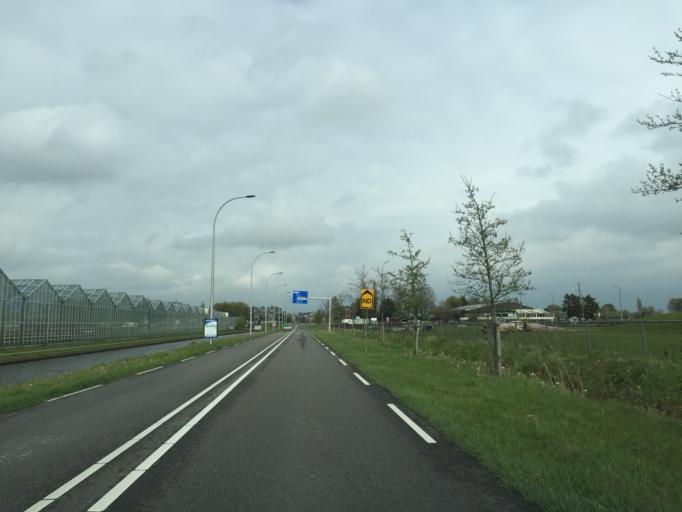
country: NL
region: South Holland
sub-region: Gemeente Den Haag
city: Ypenburg
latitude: 52.0363
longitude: 4.3974
